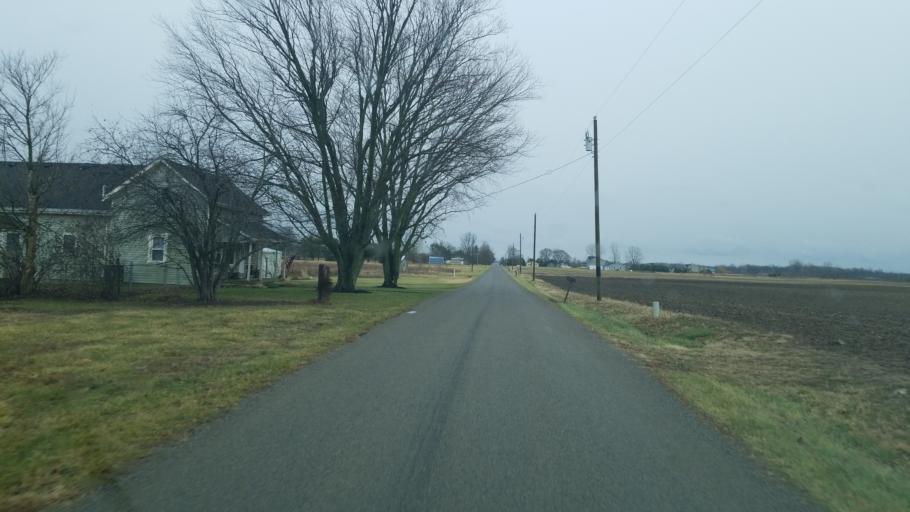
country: US
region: Ohio
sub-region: Union County
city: Marysville
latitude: 40.3329
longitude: -83.3784
